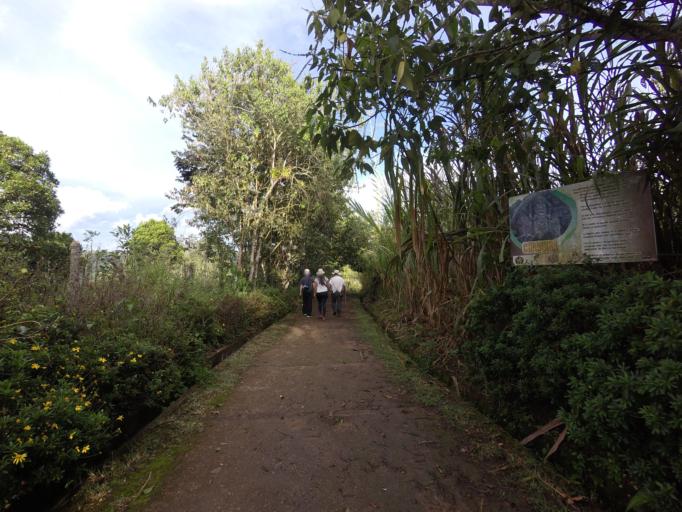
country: CO
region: Huila
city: San Agustin
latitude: 1.9032
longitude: -76.2704
